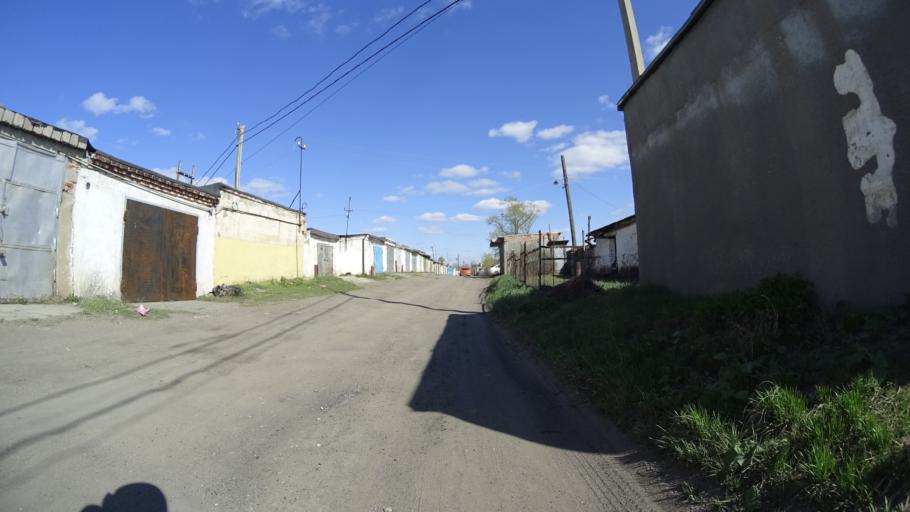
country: RU
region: Chelyabinsk
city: Troitsk
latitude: 54.0830
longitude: 61.5258
